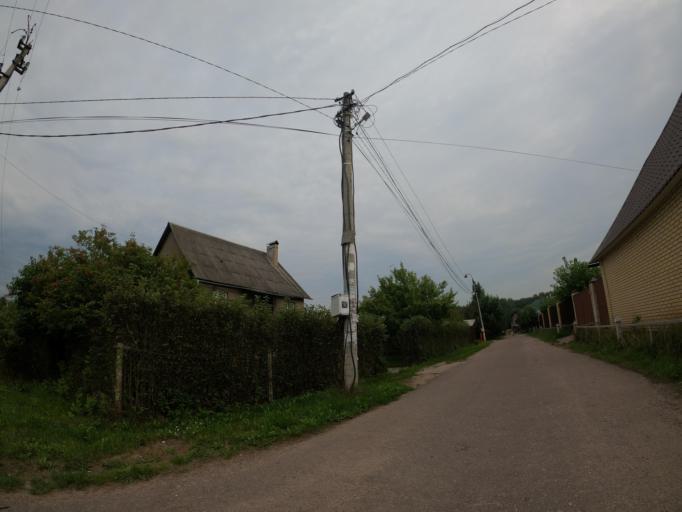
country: RU
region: Moskovskaya
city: Bykovo
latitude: 55.6538
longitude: 38.1094
